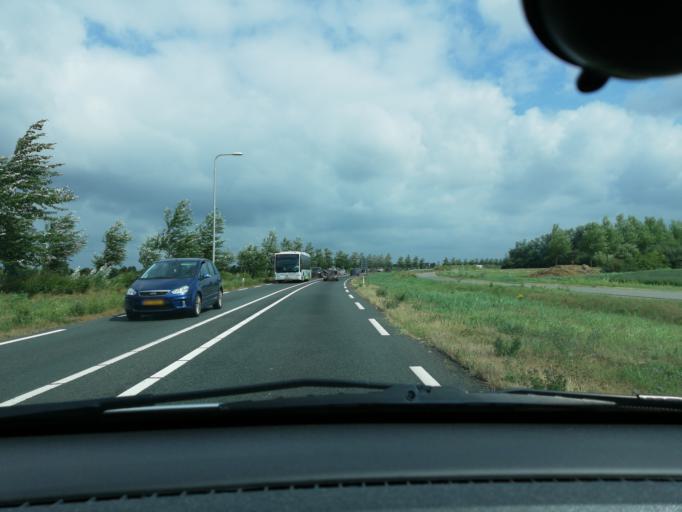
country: NL
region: Zeeland
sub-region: Gemeente Middelburg
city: Middelburg
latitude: 51.5592
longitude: 3.6001
